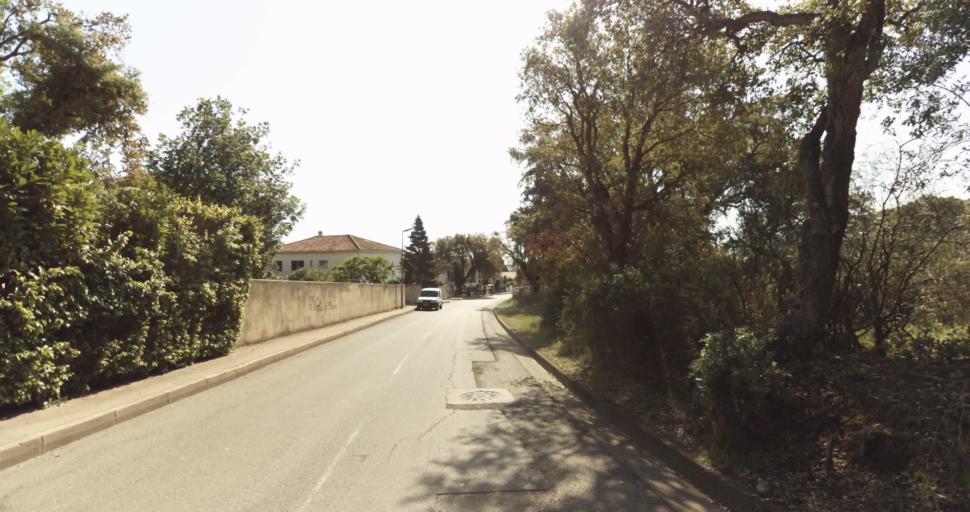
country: FR
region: Corsica
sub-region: Departement de la Haute-Corse
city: Biguglia
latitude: 42.6219
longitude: 9.4283
